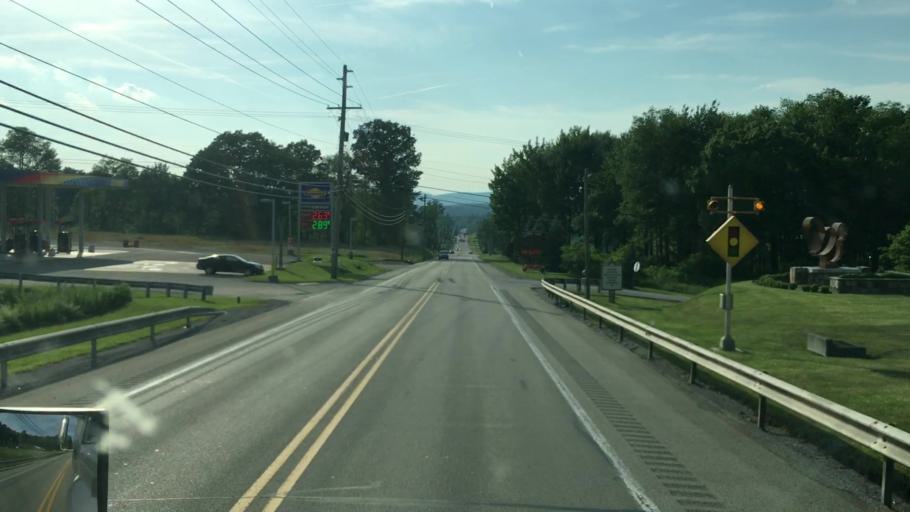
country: US
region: Pennsylvania
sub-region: Fayette County
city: Hopwood
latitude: 39.7934
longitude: -79.5373
